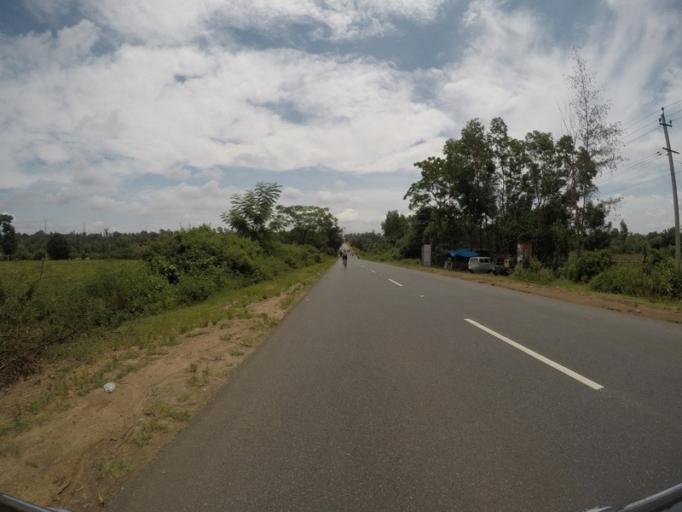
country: IN
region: Karnataka
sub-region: Kodagu
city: Kushalnagar
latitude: 12.4429
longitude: 75.9194
